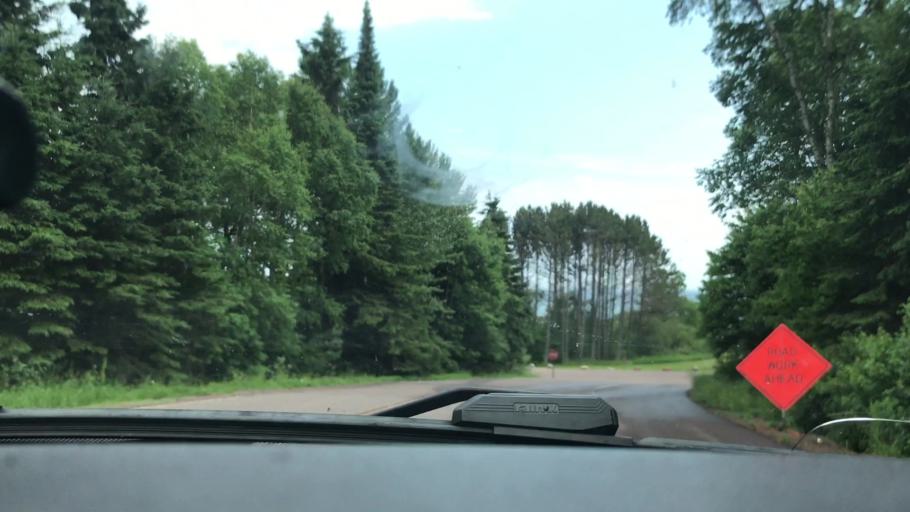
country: CA
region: Ontario
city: Neebing
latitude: 47.9643
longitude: -89.6851
